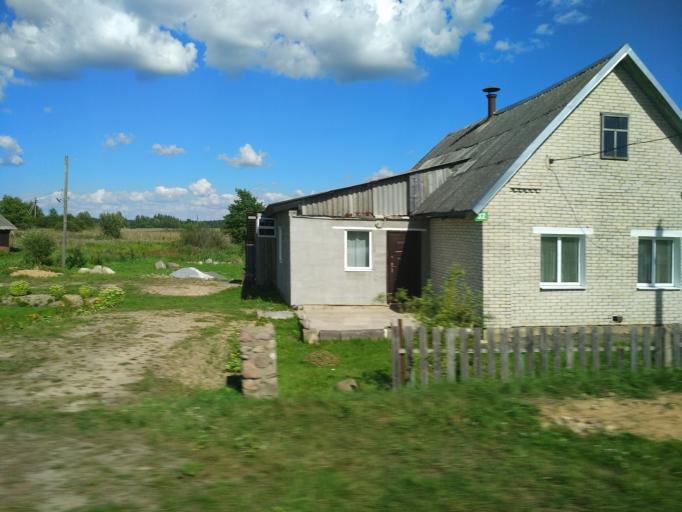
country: BY
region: Vitebsk
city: Mosar
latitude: 55.0996
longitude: 27.1988
